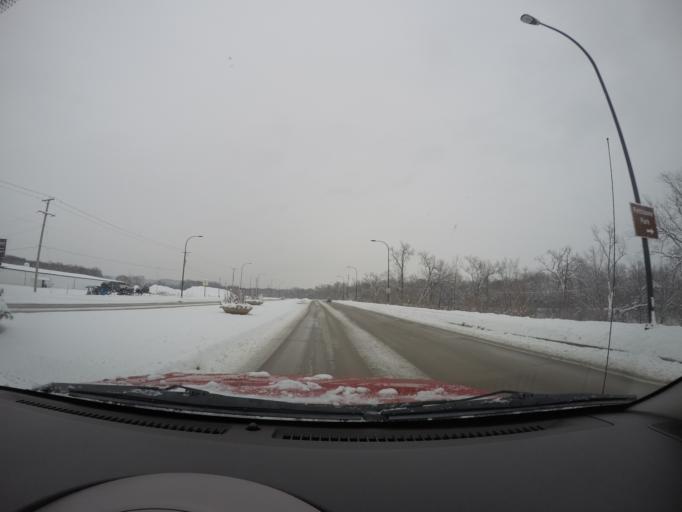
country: US
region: Wisconsin
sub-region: La Crosse County
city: La Crosse
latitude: 43.8137
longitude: -91.2656
